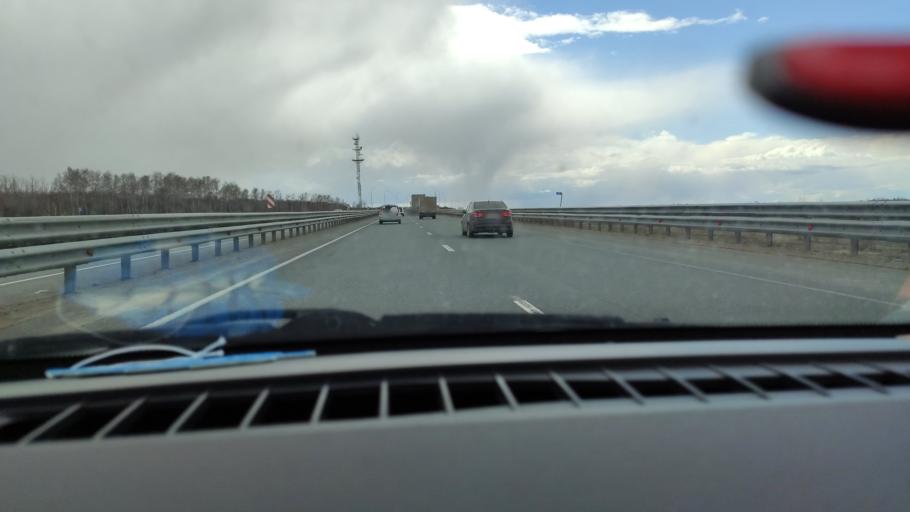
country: RU
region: Samara
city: Mezhdurechensk
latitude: 53.2775
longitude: 49.3157
